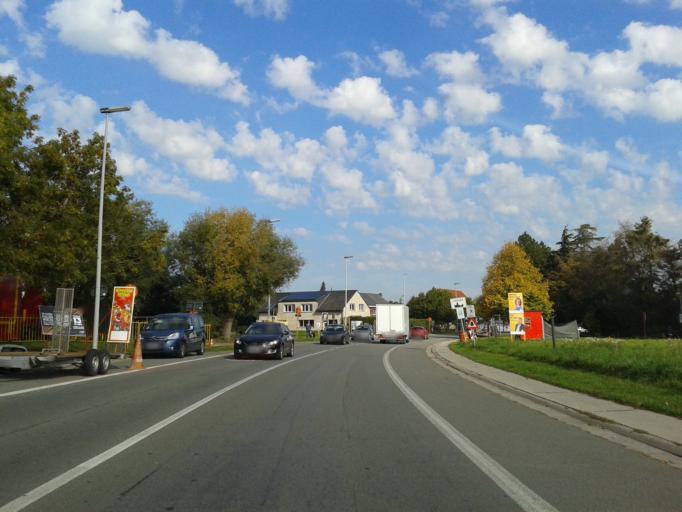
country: BE
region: Flanders
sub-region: Provincie Oost-Vlaanderen
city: Lebbeke
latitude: 51.0014
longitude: 4.1234
